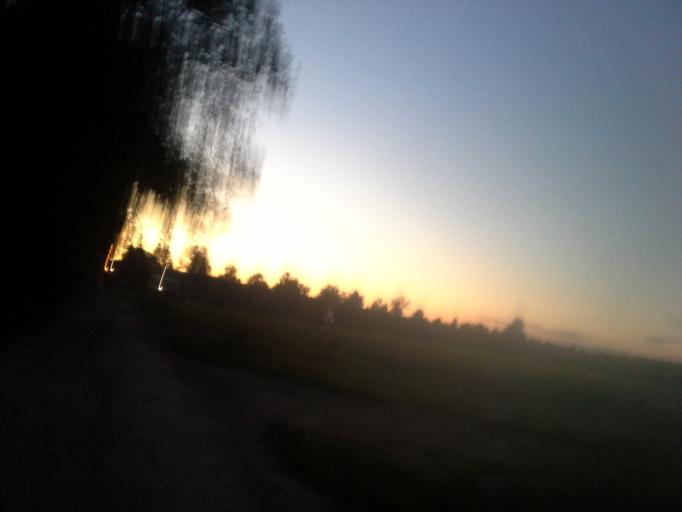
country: RU
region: Moskovskaya
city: Zhavoronki
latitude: 55.6510
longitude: 37.1165
